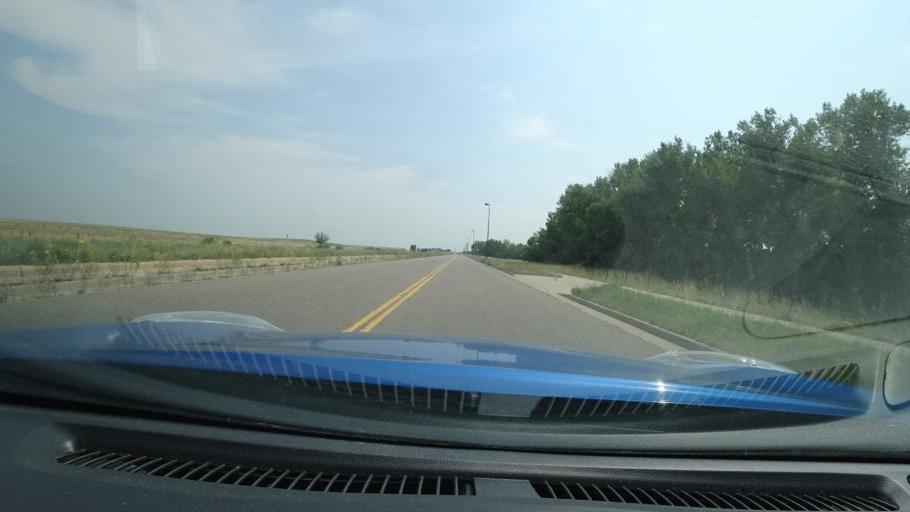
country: US
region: Colorado
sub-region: Adams County
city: Aurora
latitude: 39.7739
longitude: -104.7346
